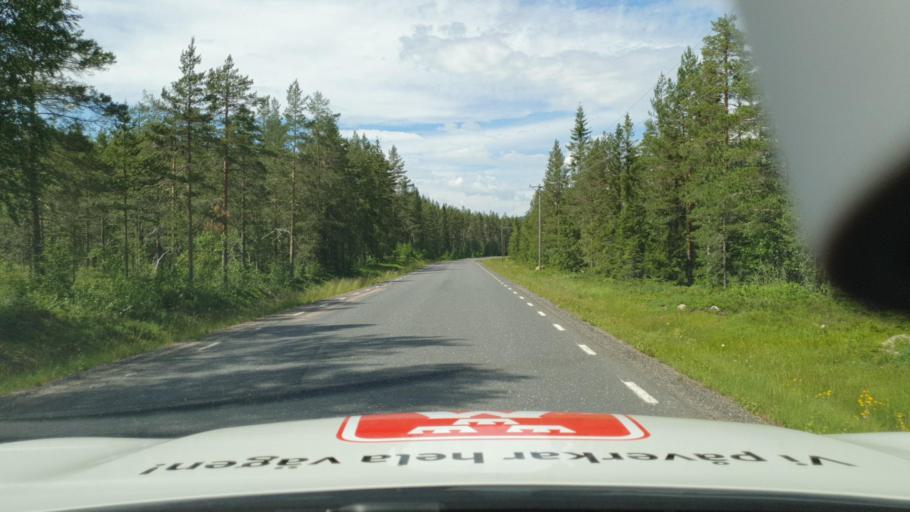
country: SE
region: Vaermland
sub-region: Torsby Kommun
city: Torsby
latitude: 60.5563
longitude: 12.7683
